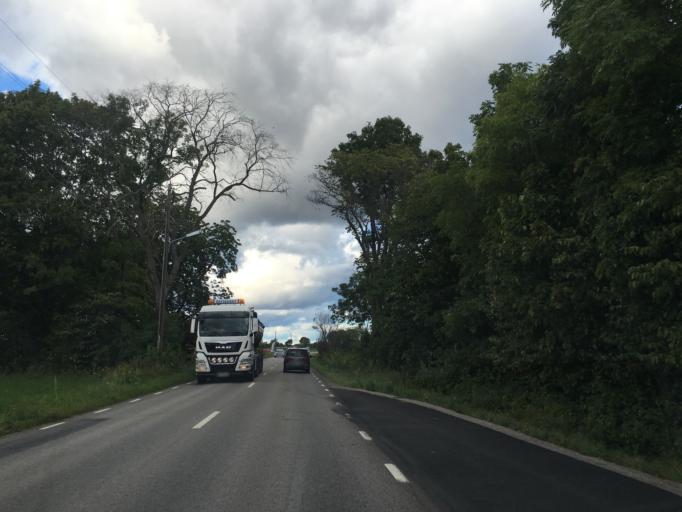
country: SE
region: Kalmar
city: Faerjestaden
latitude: 56.6439
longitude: 16.5162
